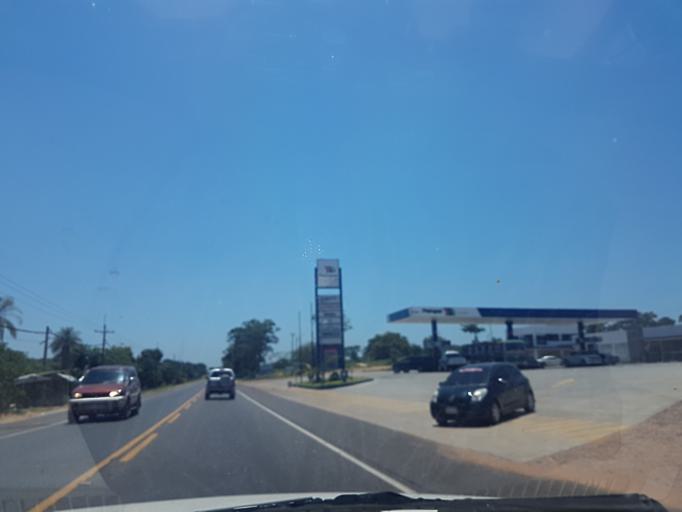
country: PY
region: Cordillera
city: Caacupe
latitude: -25.3849
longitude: -57.0543
